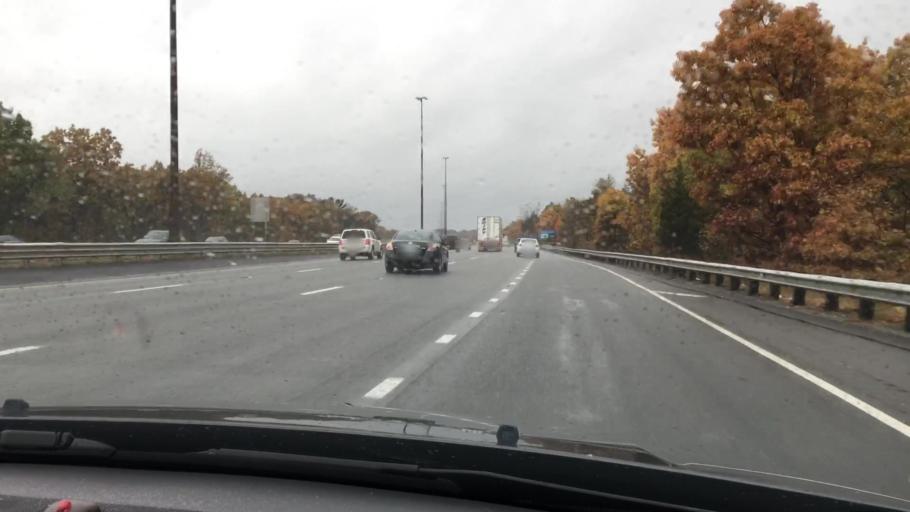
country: US
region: Massachusetts
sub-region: Middlesex County
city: Chelmsford
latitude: 42.6068
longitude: -71.3377
